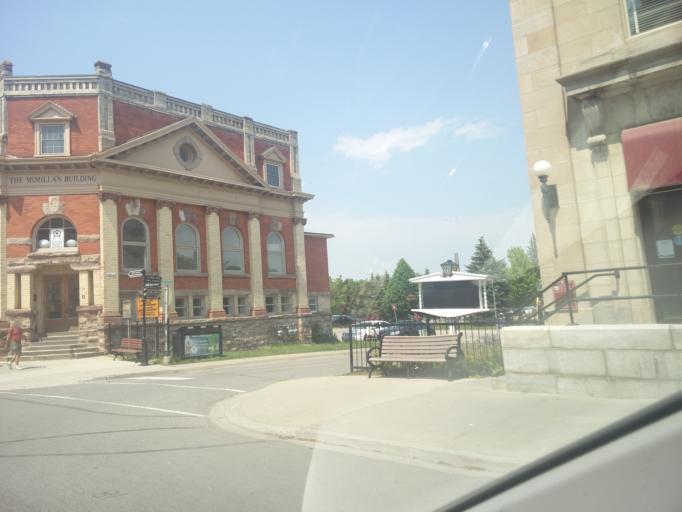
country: CA
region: Ontario
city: Perth
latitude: 44.8992
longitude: -76.2486
